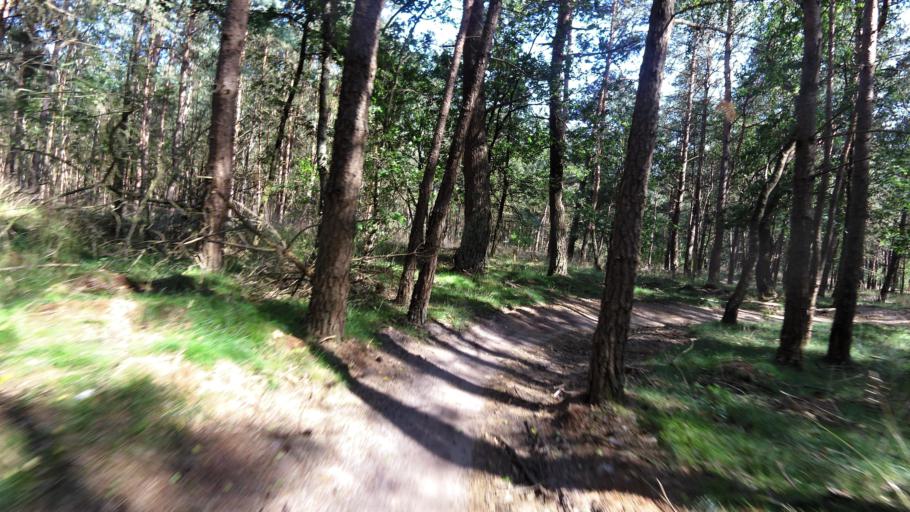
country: NL
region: Gelderland
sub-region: Gemeente Arnhem
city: Gulden Bodem
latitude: 52.0229
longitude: 5.9161
